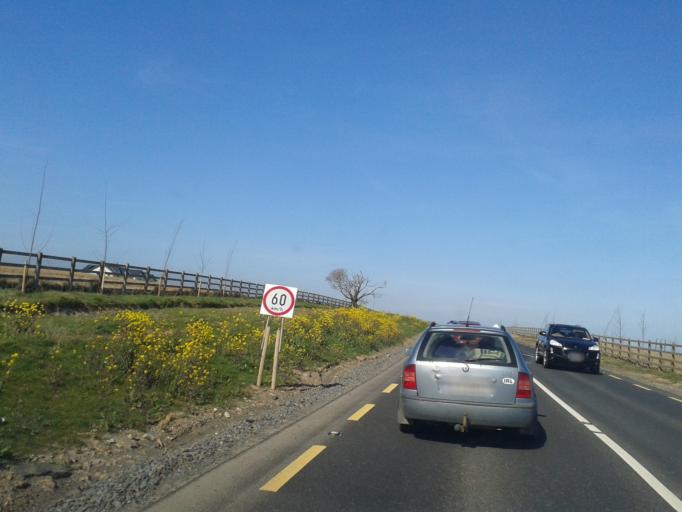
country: IE
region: Leinster
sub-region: Wicklow
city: Arklow
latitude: 52.8443
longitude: -6.1142
